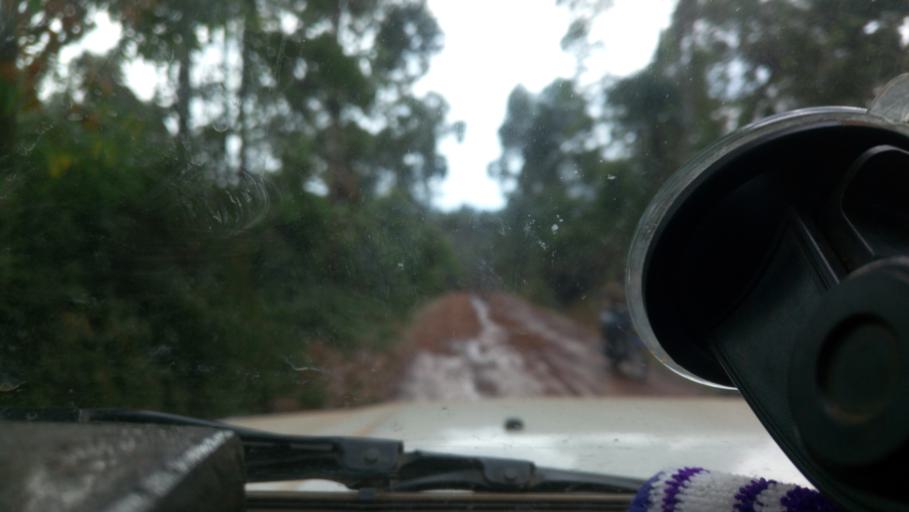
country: KE
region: Kericho
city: Litein
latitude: -0.5912
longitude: 35.2019
